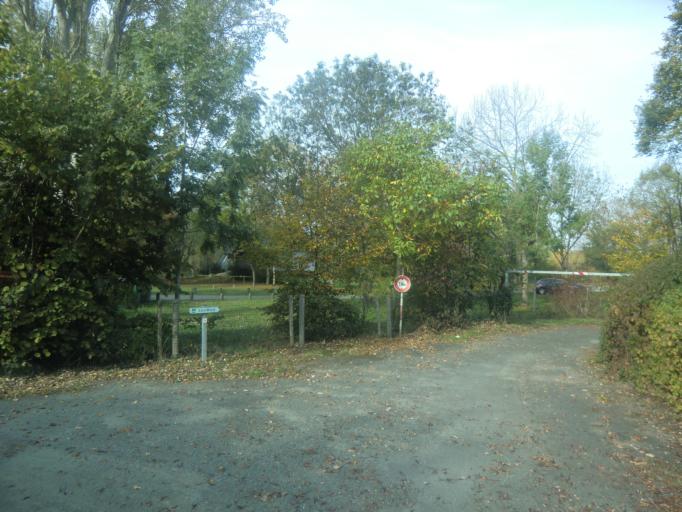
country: FR
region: Pays de la Loire
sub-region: Departement de Maine-et-Loire
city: Villebernier
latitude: 47.2412
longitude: -0.0225
